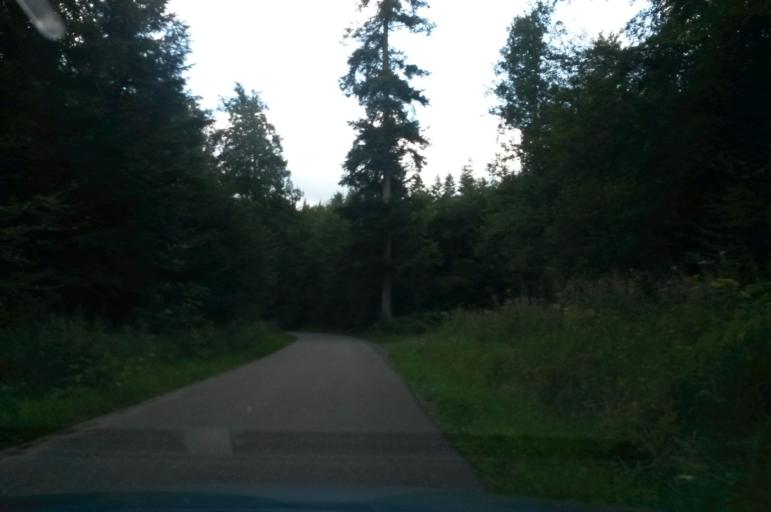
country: DE
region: Baden-Wuerttemberg
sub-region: Karlsruhe Region
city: Bad Herrenalb
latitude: 48.8379
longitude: 8.4592
